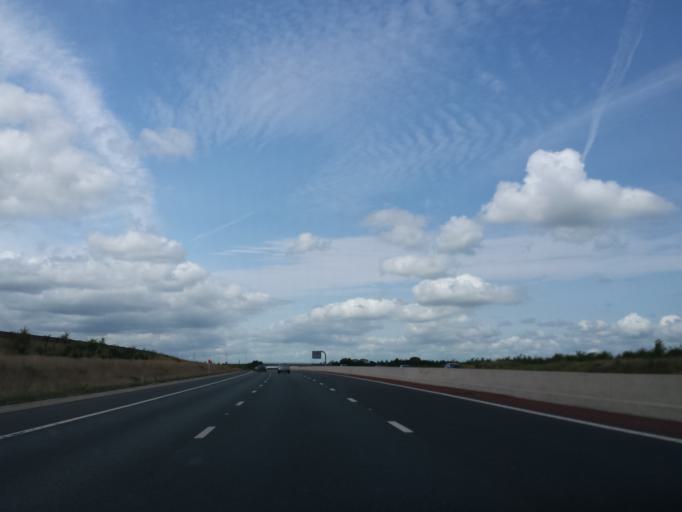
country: GB
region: England
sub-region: North Yorkshire
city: Bedale
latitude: 54.2676
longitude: -1.5220
